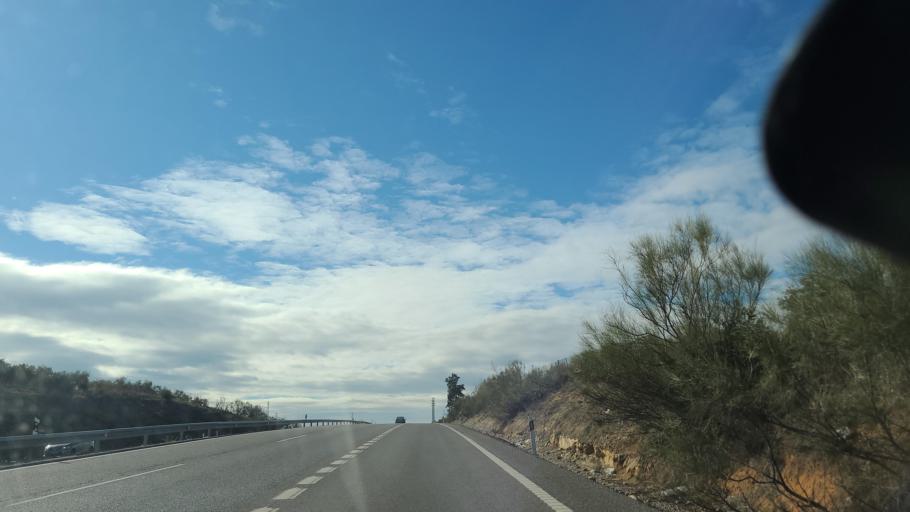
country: ES
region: Andalusia
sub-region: Provincia de Jaen
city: Espeluy
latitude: 38.0701
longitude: -3.8705
